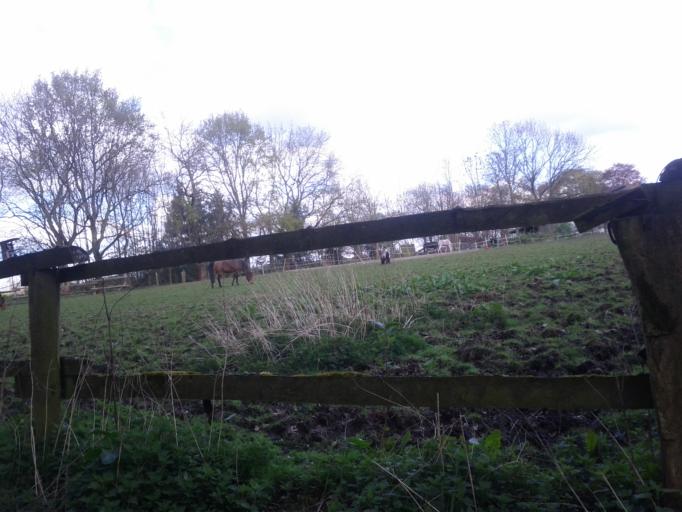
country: DE
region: North Rhine-Westphalia
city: Lanstrop
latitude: 51.5708
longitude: 7.5519
